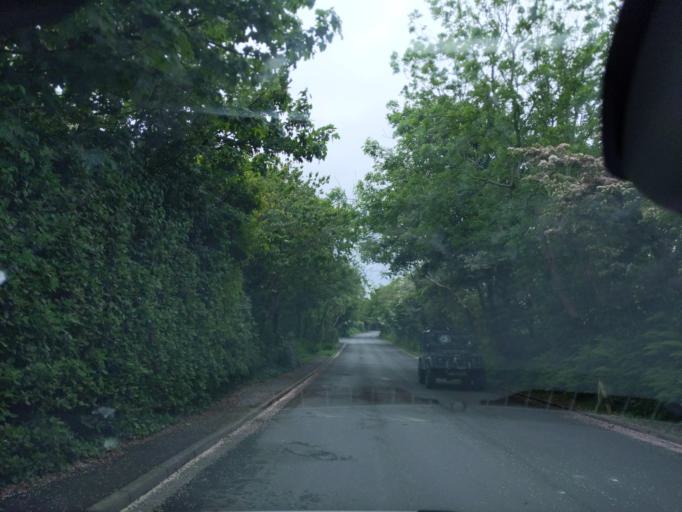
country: IM
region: Douglas
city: Douglas
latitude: 54.1390
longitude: -4.5620
